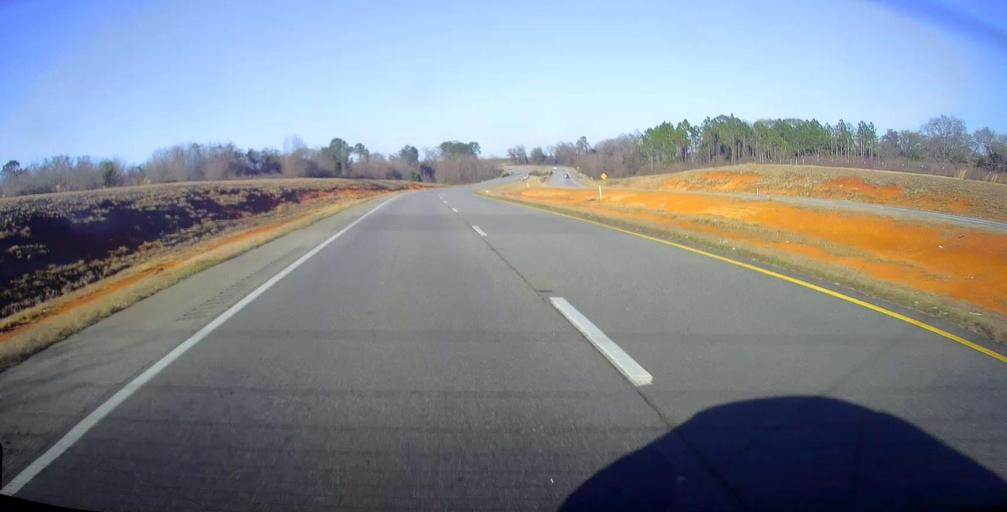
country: US
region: Georgia
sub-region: Sumter County
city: Americus
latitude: 31.9709
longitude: -84.2505
